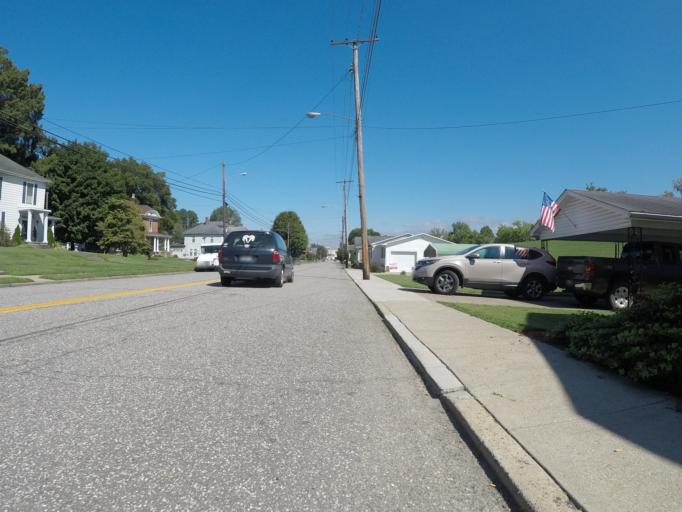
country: US
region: Kentucky
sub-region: Boyd County
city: Catlettsburg
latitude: 38.4095
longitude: -82.5983
